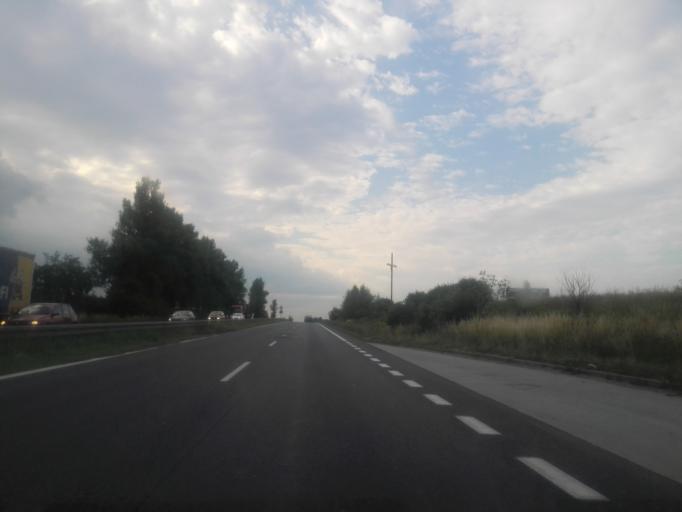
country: PL
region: Silesian Voivodeship
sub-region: Powiat bedzinski
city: Siewierz
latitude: 50.4998
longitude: 19.2014
